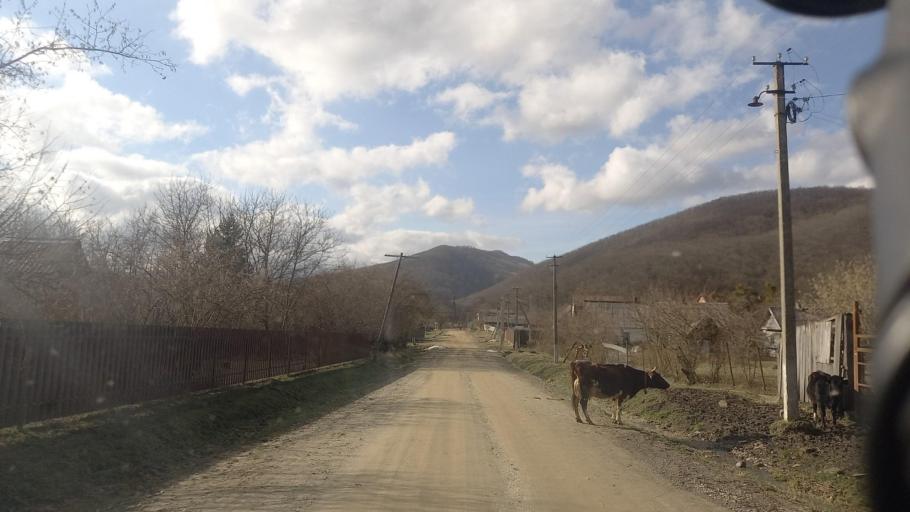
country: RU
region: Krasnodarskiy
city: Smolenskaya
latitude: 44.6046
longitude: 38.8523
